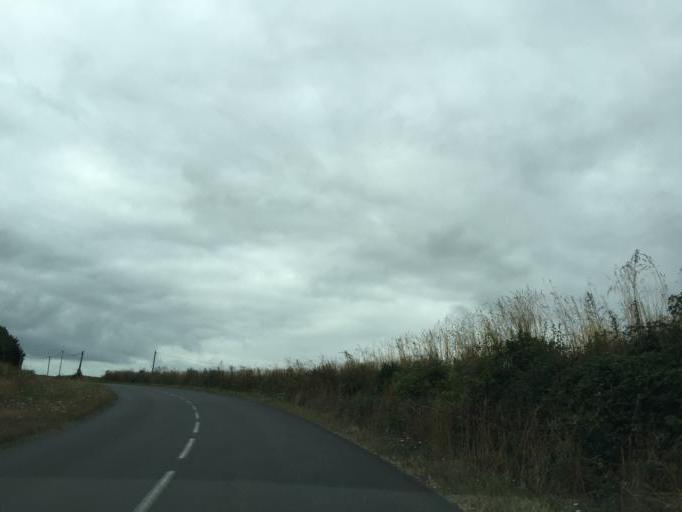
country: FR
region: Brittany
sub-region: Departement des Cotes-d'Armor
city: Jugon-les-Lacs
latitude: 48.3905
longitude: -2.3491
